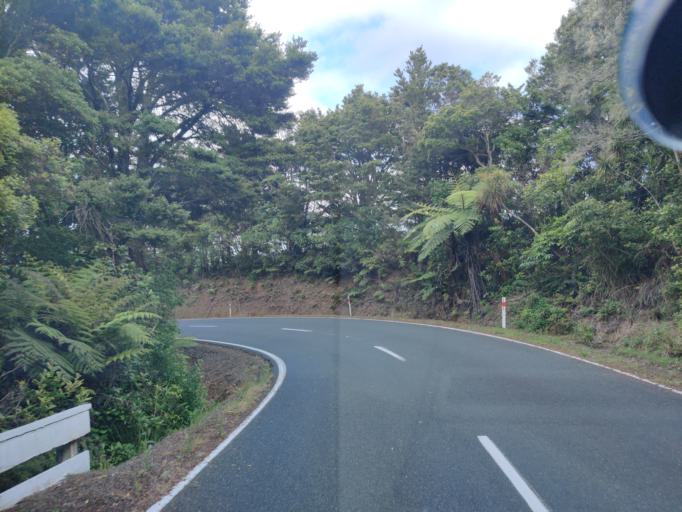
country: NZ
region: Northland
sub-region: Whangarei
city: Ngunguru
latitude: -35.5775
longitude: 174.4090
